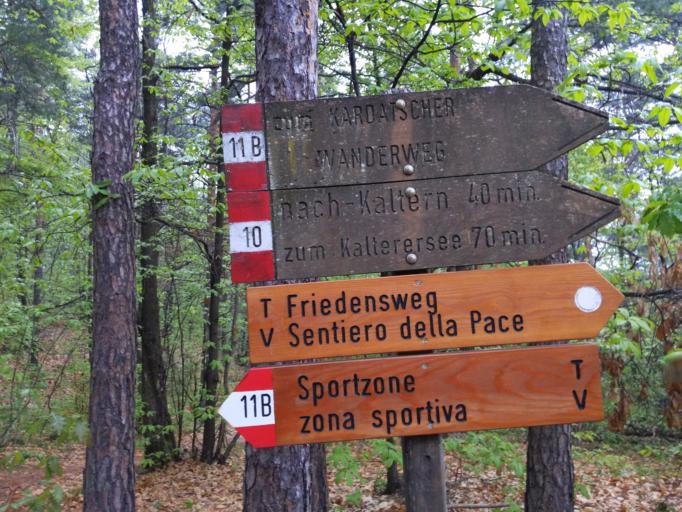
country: IT
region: Trentino-Alto Adige
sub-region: Bolzano
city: Caldaro sulla Strada del Vino
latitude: 46.3964
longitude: 11.2414
